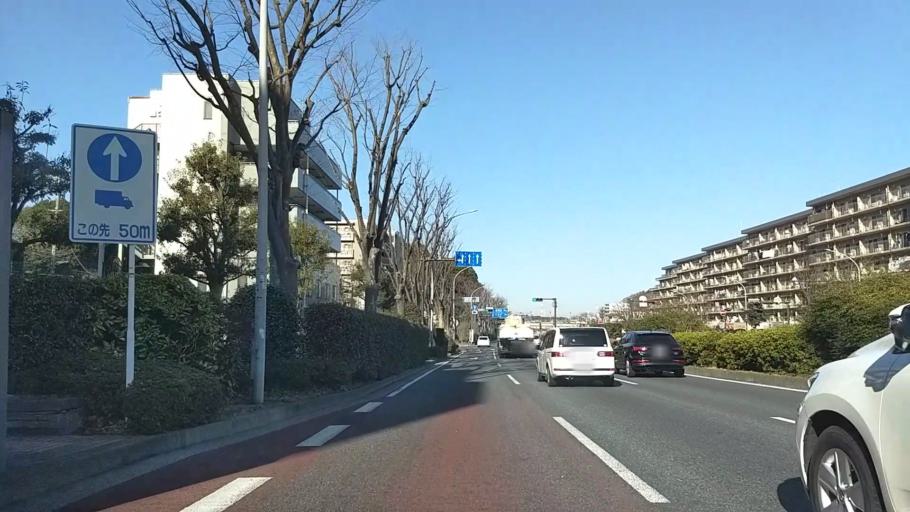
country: JP
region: Kanagawa
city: Yokohama
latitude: 35.4024
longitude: 139.5735
